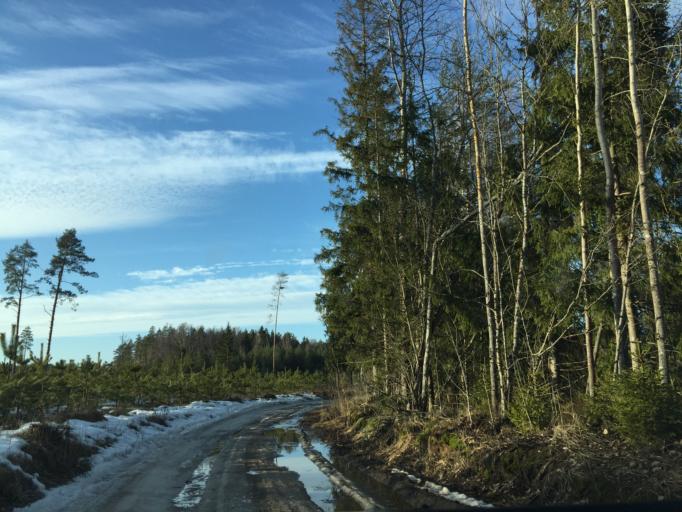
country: LV
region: Lecava
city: Iecava
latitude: 56.6902
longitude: 24.0774
